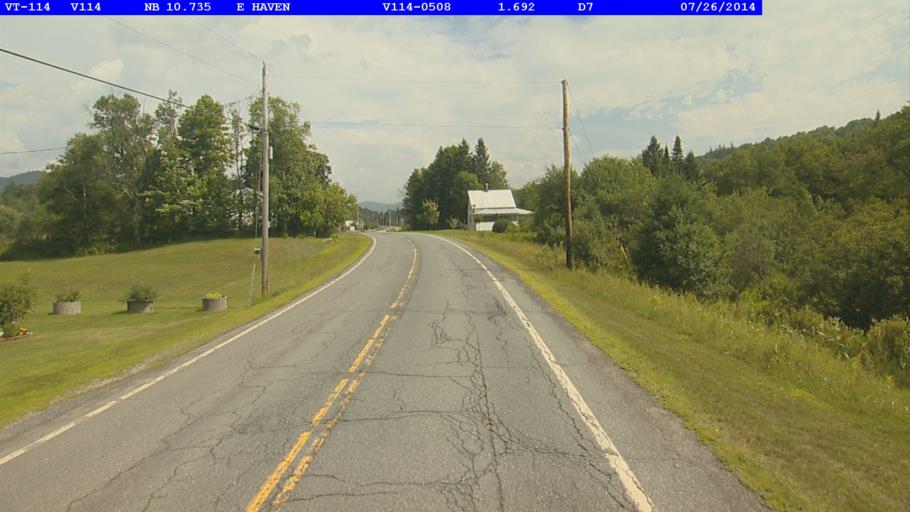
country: US
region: Vermont
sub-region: Caledonia County
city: Lyndonville
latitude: 44.6629
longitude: -71.8893
